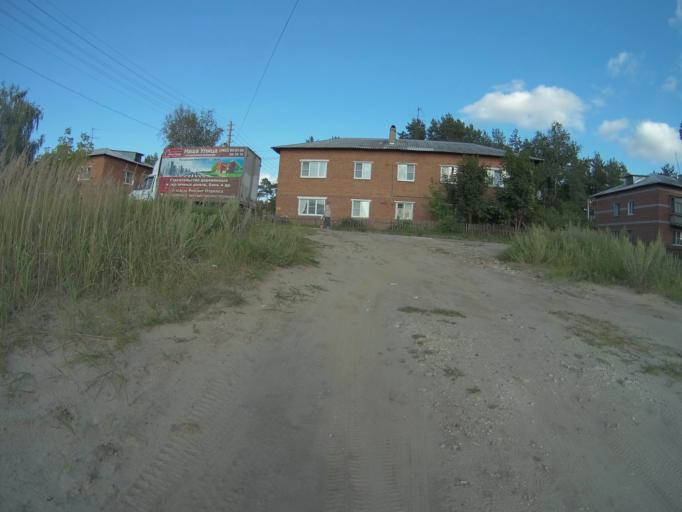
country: RU
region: Vladimir
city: Kommunar
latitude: 56.1202
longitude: 40.4568
